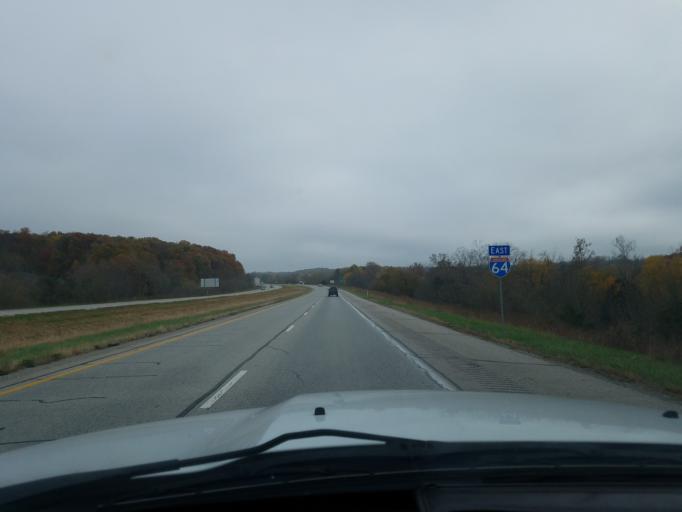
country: US
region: Indiana
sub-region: Harrison County
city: Corydon
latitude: 38.2397
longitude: -86.1219
